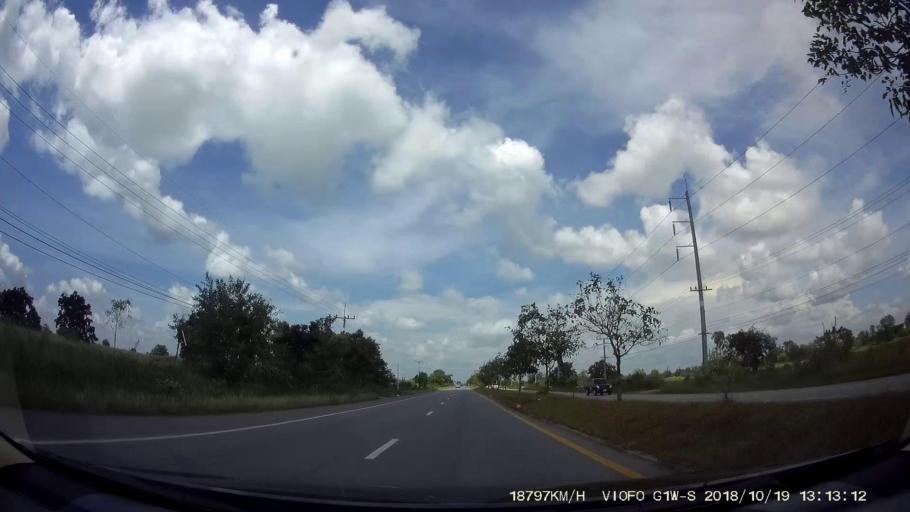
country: TH
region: Nakhon Ratchasima
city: Dan Khun Thot
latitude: 15.3565
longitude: 101.8285
